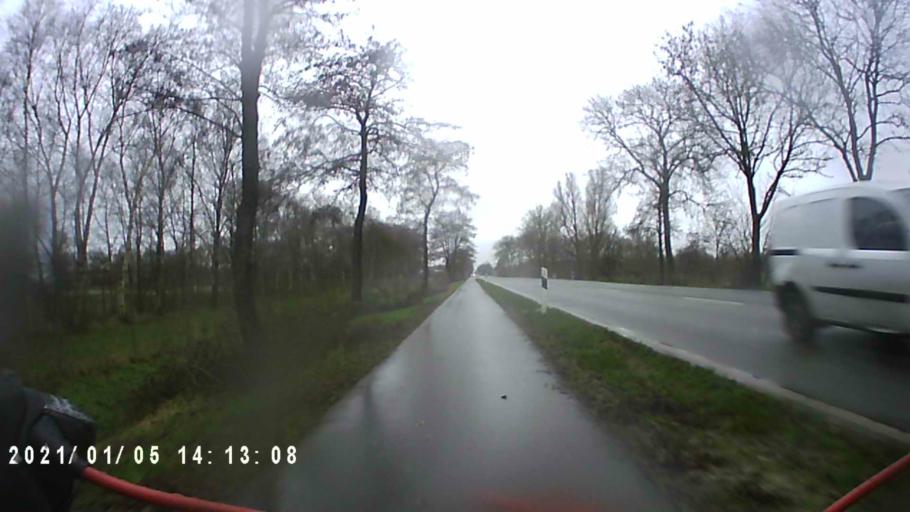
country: DE
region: Lower Saxony
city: Weener
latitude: 53.1713
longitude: 7.3251
